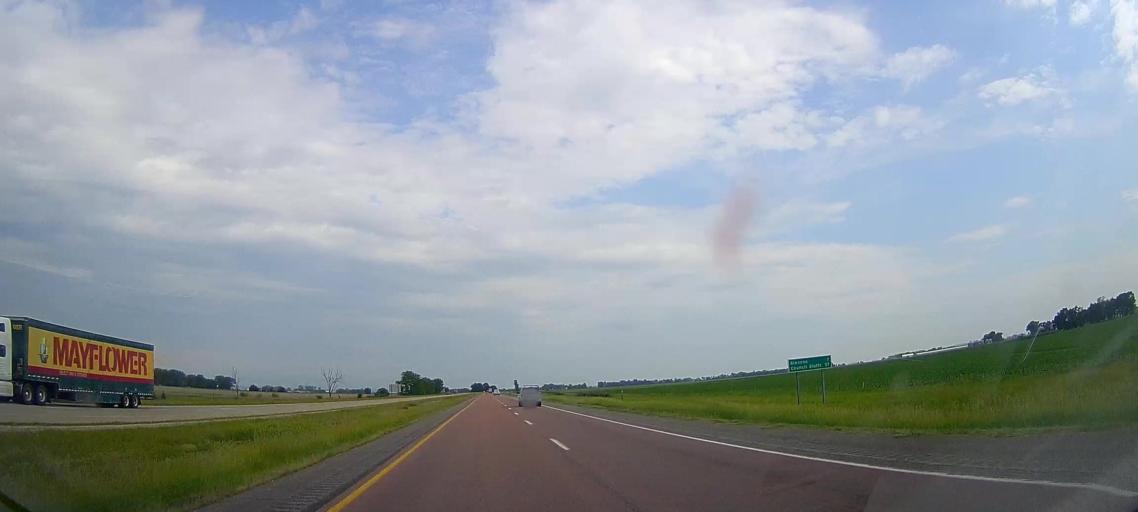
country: US
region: Iowa
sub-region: Monona County
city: Onawa
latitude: 42.0153
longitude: -96.1233
